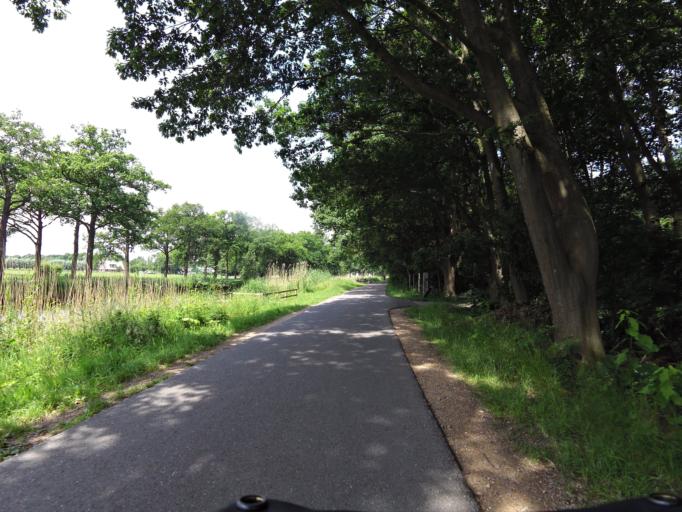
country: NL
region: Gelderland
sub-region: Gemeente Brummen
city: Eerbeek
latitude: 52.1263
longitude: 6.0480
